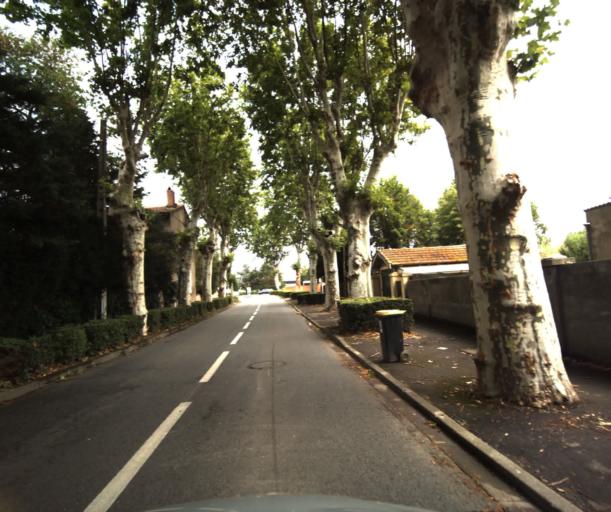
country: FR
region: Midi-Pyrenees
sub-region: Departement de la Haute-Garonne
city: Portet-sur-Garonne
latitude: 43.5256
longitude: 1.4089
